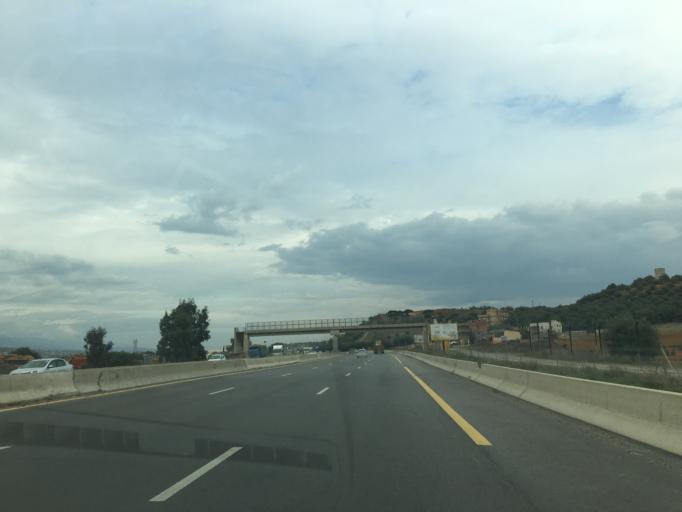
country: DZ
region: Bouira
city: Bouira
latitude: 36.3109
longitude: 4.0398
